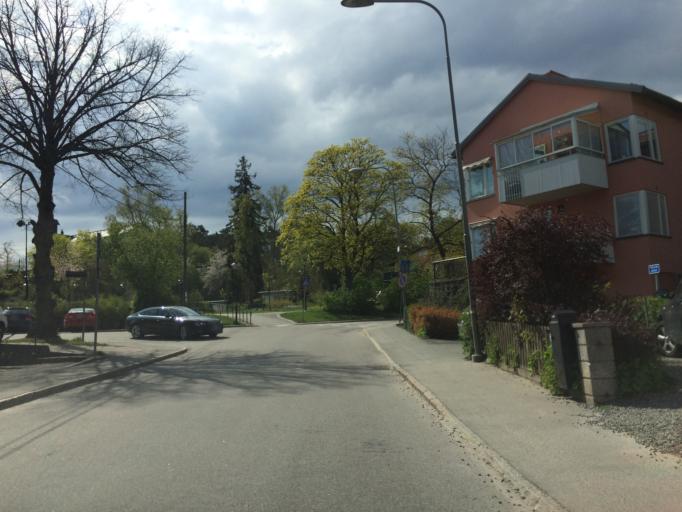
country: SE
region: Stockholm
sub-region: Huddinge Kommun
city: Segeltorp
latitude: 59.3020
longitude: 17.9571
